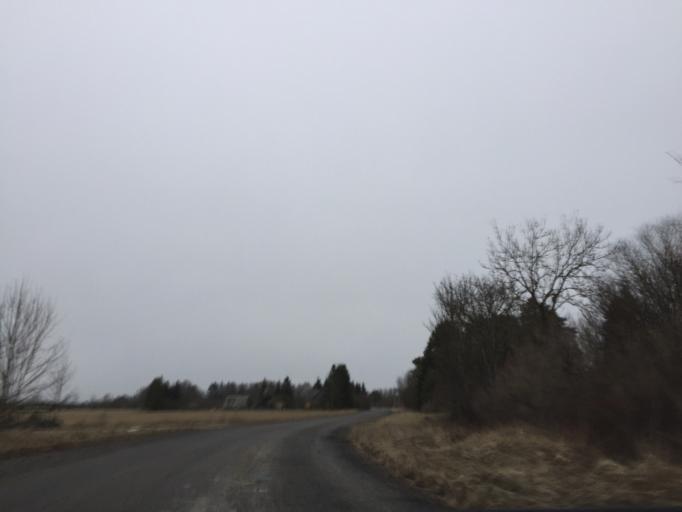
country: EE
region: Laeaene
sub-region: Lihula vald
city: Lihula
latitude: 58.6349
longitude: 23.6298
